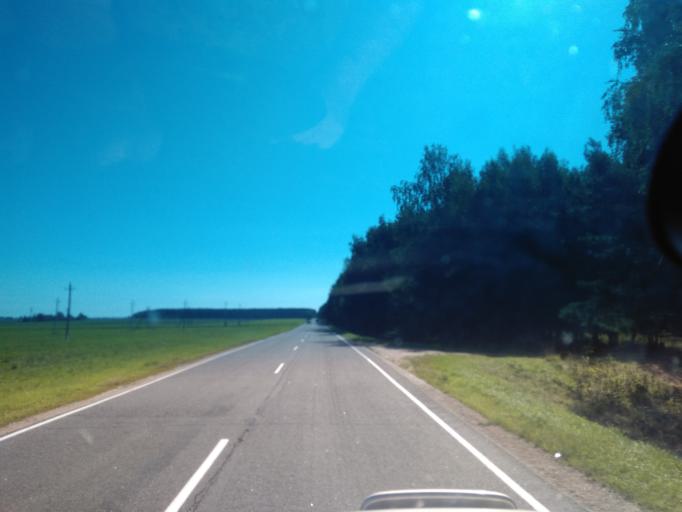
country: BY
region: Minsk
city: Stan'kava
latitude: 53.6252
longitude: 27.2732
